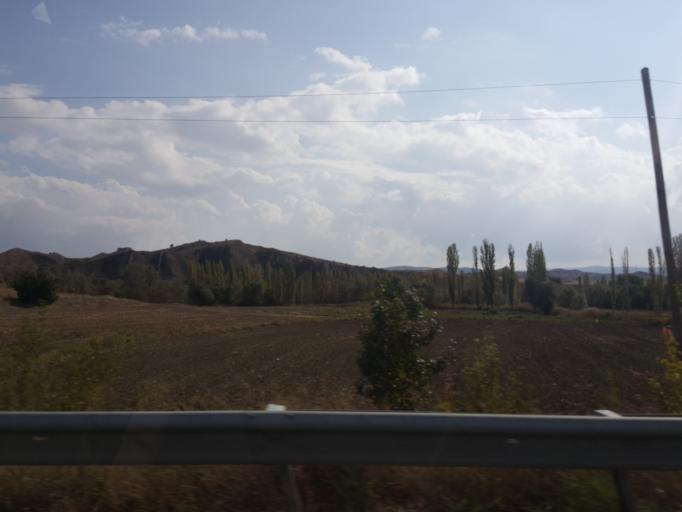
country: TR
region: Corum
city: Sungurlu
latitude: 40.1814
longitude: 34.4798
